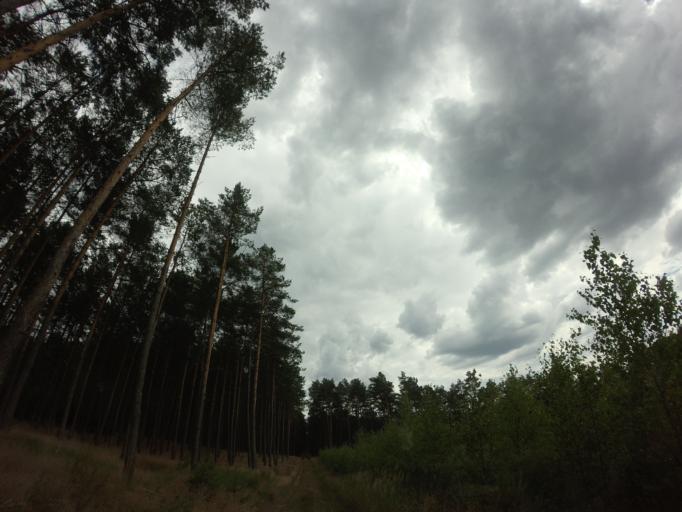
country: PL
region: West Pomeranian Voivodeship
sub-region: Powiat choszczenski
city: Drawno
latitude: 53.1574
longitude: 15.7374
